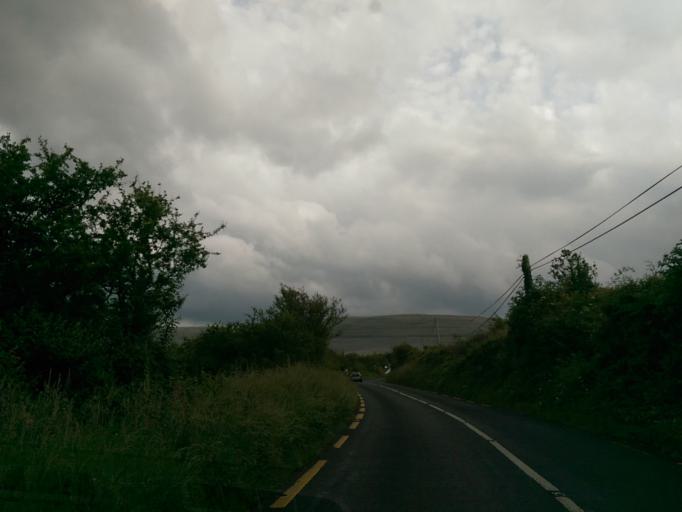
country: IE
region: Connaught
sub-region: County Galway
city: Bearna
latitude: 53.1233
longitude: -9.0756
